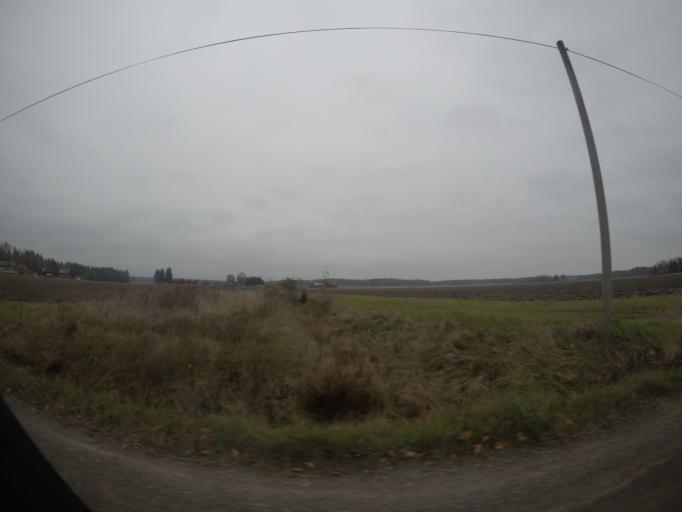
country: SE
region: Vaestmanland
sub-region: Kopings Kommun
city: Koping
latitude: 59.5997
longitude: 16.0771
